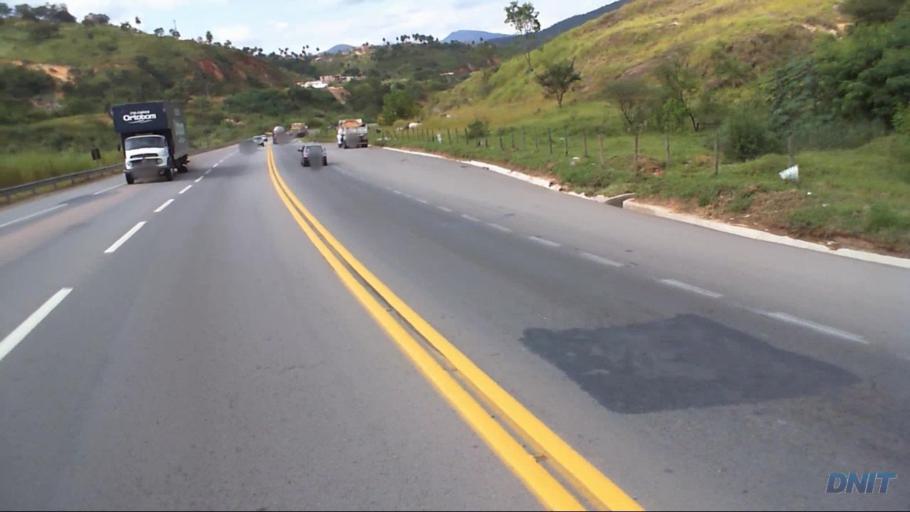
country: BR
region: Minas Gerais
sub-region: Santa Luzia
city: Santa Luzia
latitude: -19.8383
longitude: -43.8844
